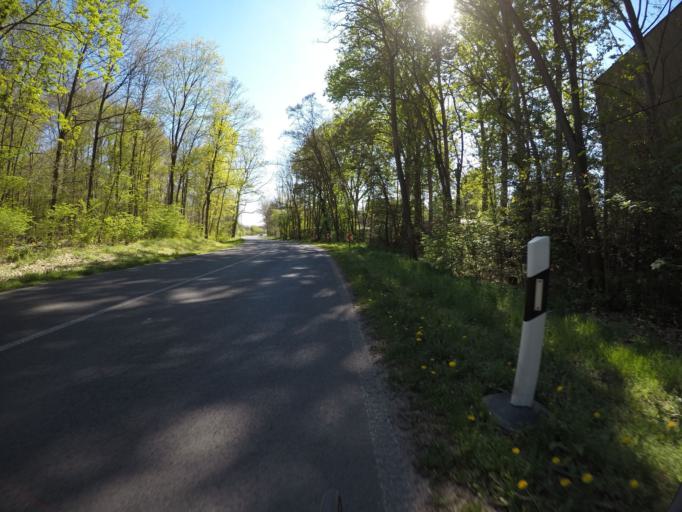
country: DE
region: Brandenburg
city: Rehfelde
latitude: 52.5404
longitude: 13.9363
